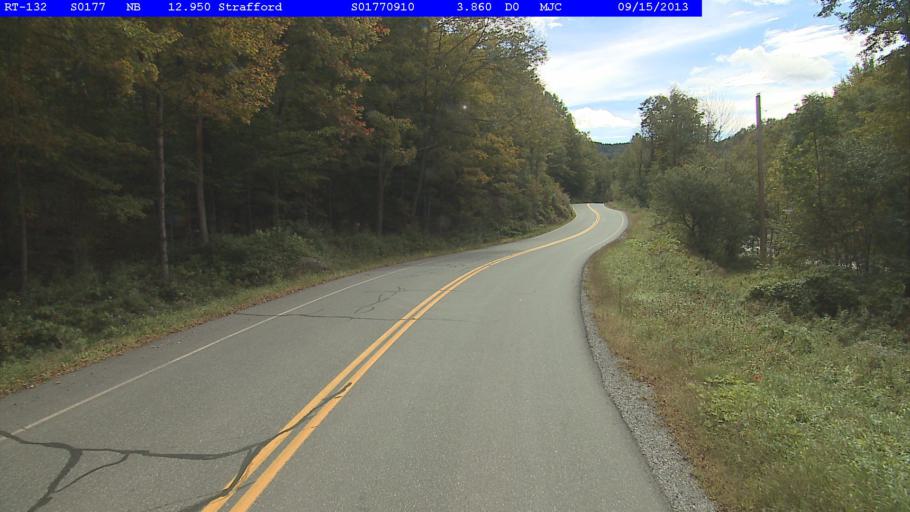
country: US
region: New Hampshire
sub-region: Grafton County
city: Hanover
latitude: 43.8366
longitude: -72.3353
